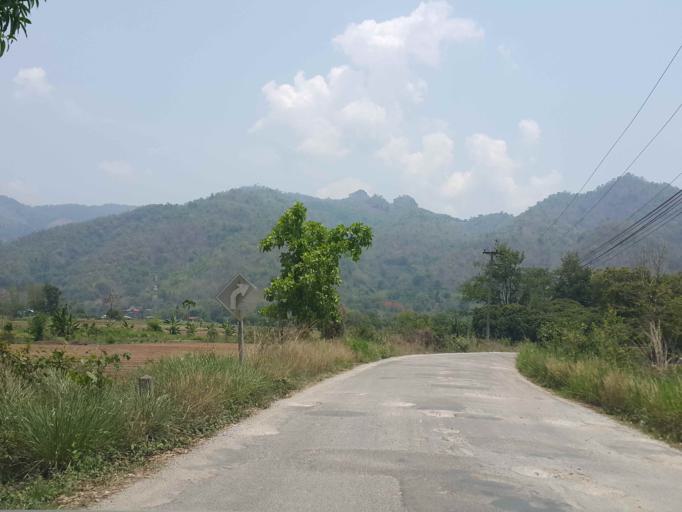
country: TH
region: Chiang Mai
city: Mae Taeng
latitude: 19.2097
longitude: 98.8547
